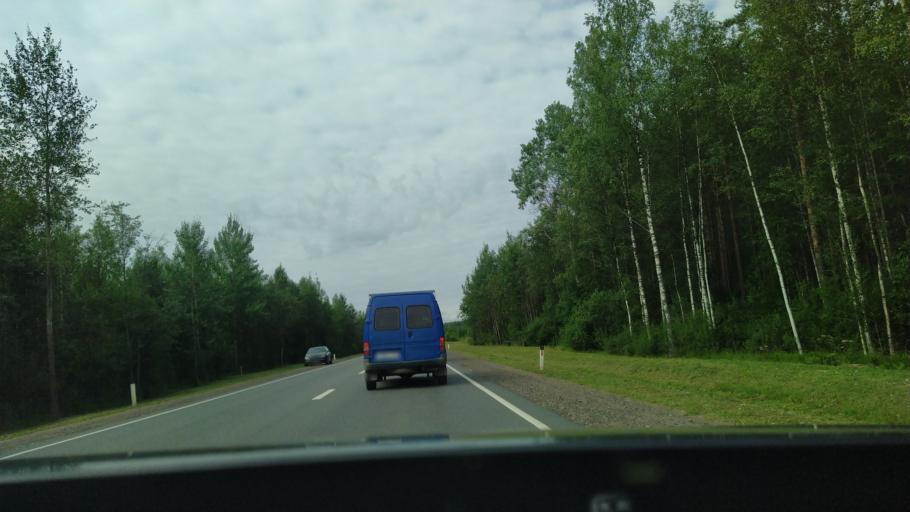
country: RU
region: Leningrad
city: Ul'yanovka
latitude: 59.6096
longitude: 30.7676
